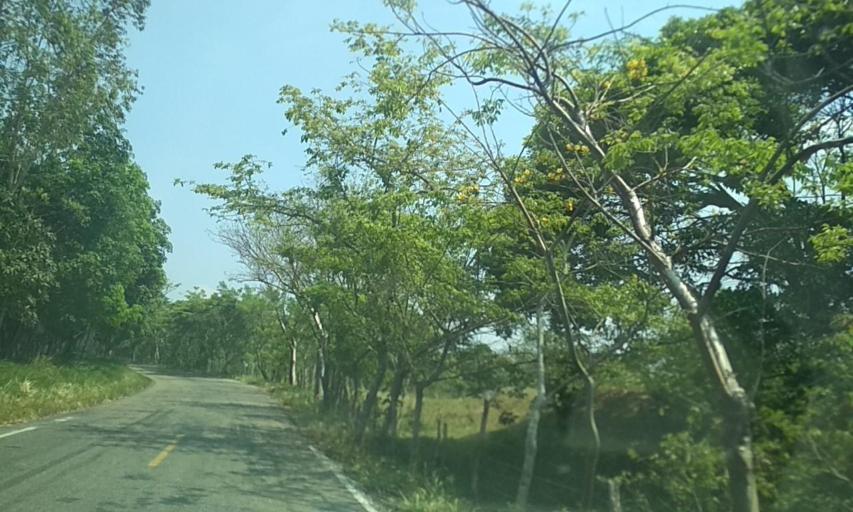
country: MX
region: Tabasco
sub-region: Huimanguillo
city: C-41 (Licenciado Carlos A. Madrazo)
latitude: 17.8414
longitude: -93.5217
